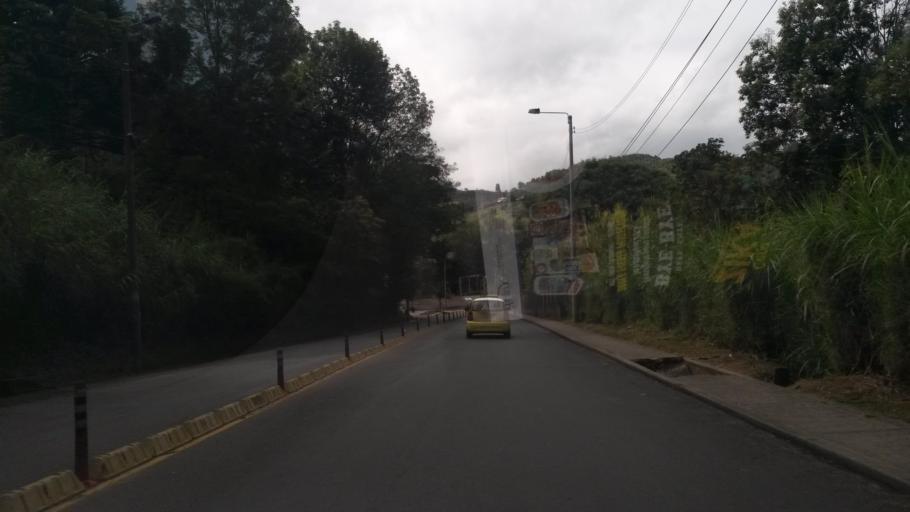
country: CO
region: Cauca
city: Popayan
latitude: 2.4749
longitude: -76.5793
